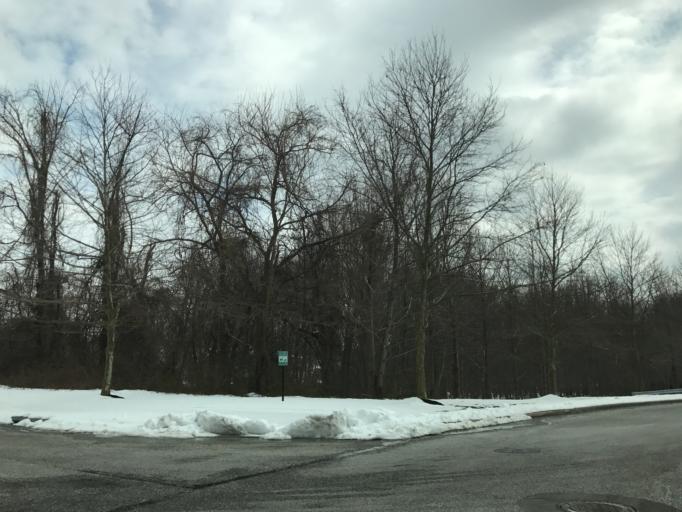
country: US
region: Maryland
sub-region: Harford County
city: Bel Air North
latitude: 39.5737
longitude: -76.3791
